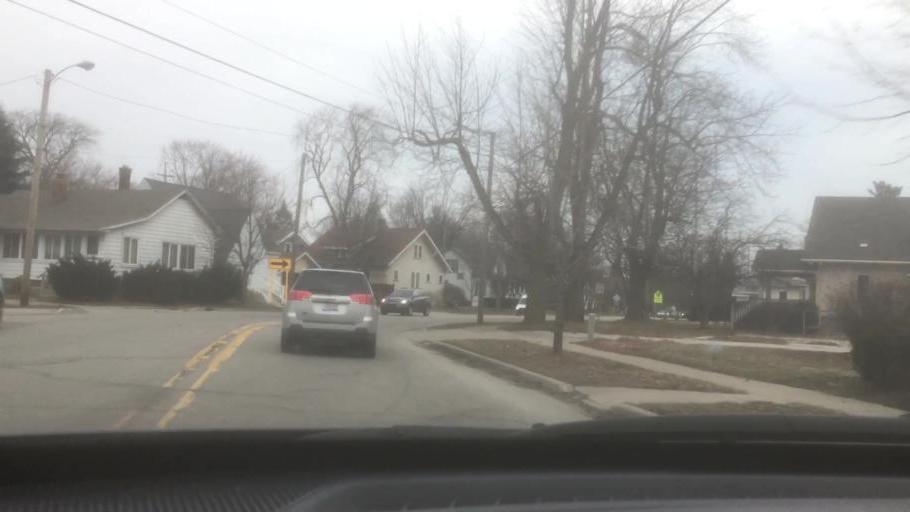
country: US
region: Michigan
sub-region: Bay County
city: Bay City
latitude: 43.5916
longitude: -83.8669
